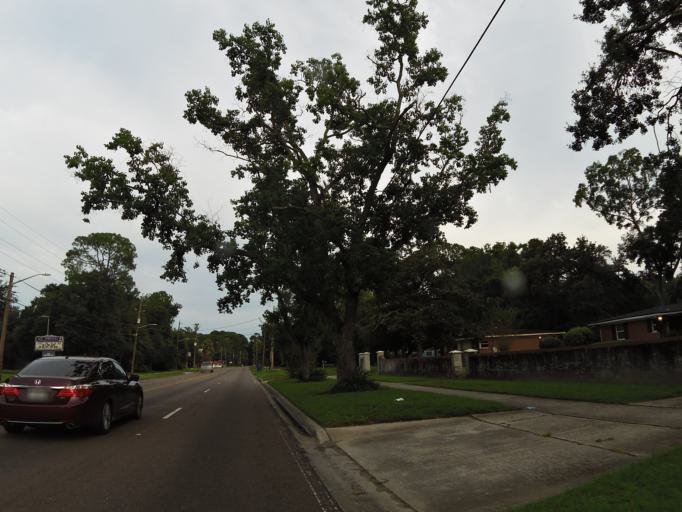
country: US
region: Florida
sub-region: Duval County
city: Jacksonville
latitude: 30.3791
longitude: -81.6941
